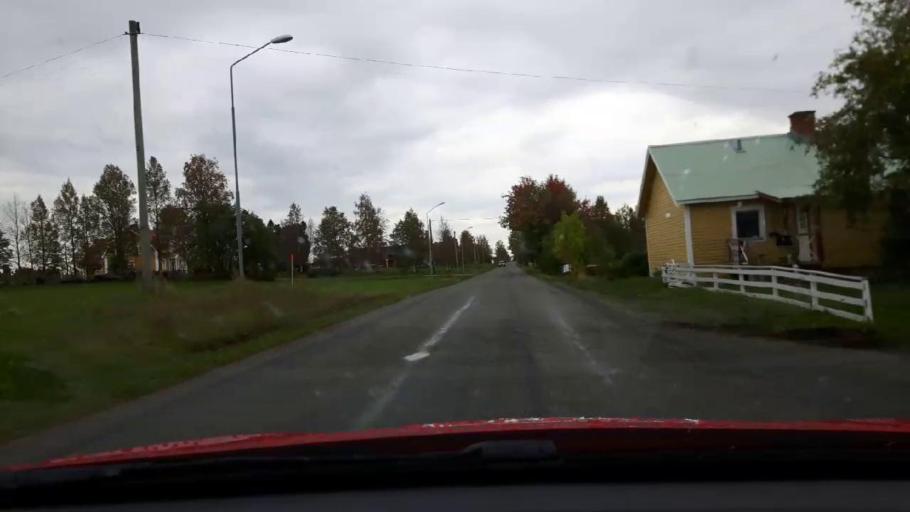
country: SE
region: Jaemtland
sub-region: Bergs Kommun
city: Hoverberg
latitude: 62.9639
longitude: 14.4896
